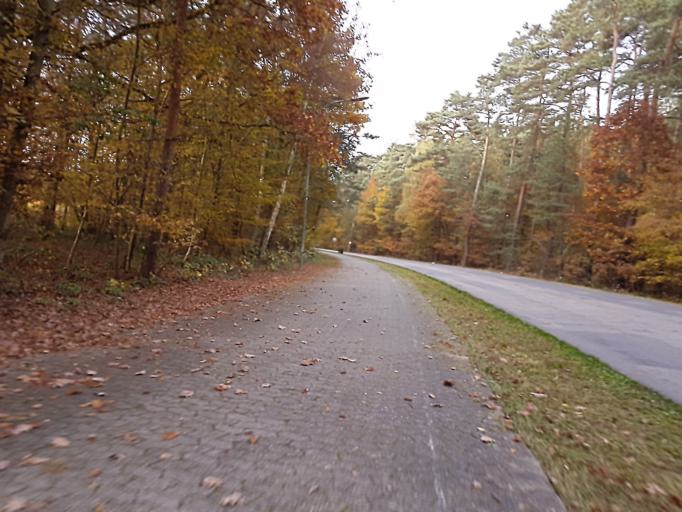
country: DE
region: Bavaria
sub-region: Regierungsbezirk Unterfranken
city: Worth am Main
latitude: 49.8135
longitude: 9.1464
